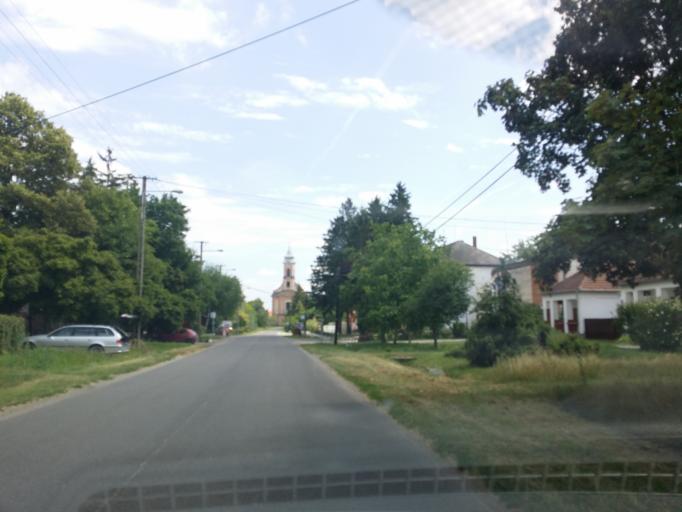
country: HU
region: Heves
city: Tiszanana
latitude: 47.5903
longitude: 20.5942
